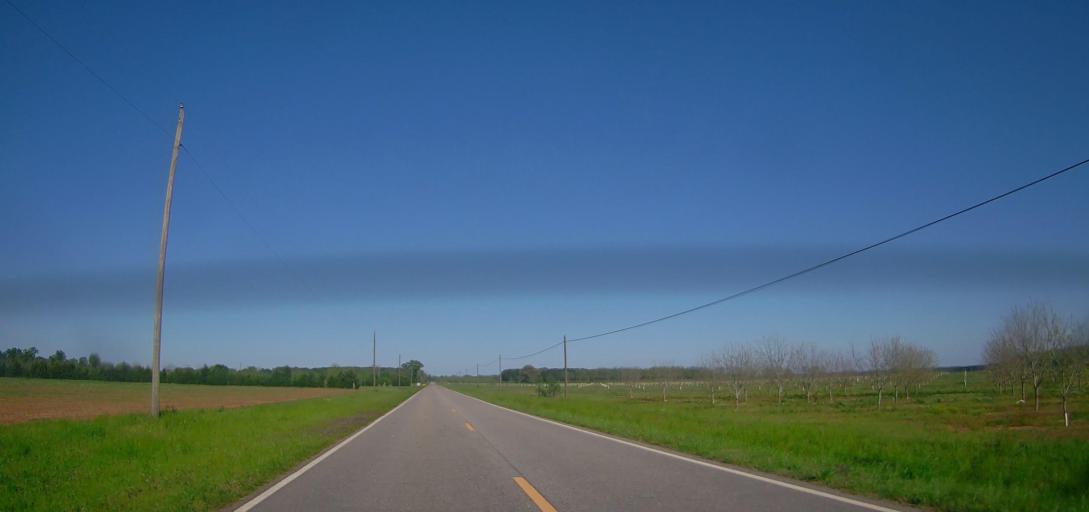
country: US
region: Georgia
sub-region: Houston County
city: Perry
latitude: 32.4515
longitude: -83.6644
